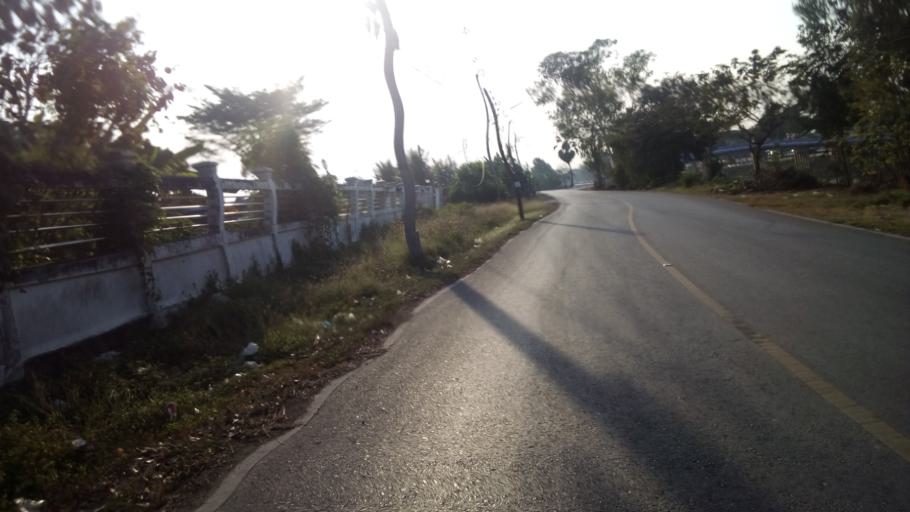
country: TH
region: Pathum Thani
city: Nong Suea
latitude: 14.0584
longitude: 100.8430
